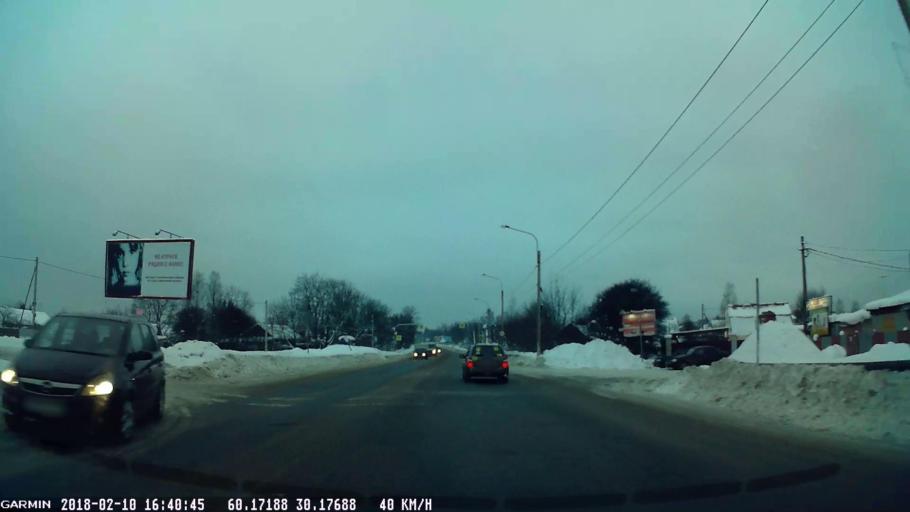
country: RU
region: Leningrad
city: Sertolovo
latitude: 60.1618
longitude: 30.1838
